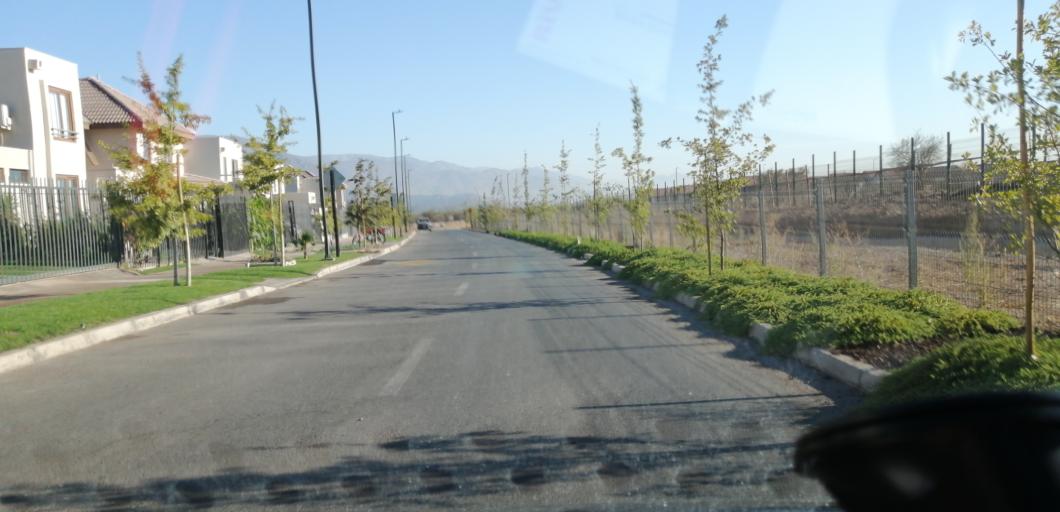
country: CL
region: Santiago Metropolitan
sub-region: Provincia de Santiago
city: Lo Prado
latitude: -33.4680
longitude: -70.8598
